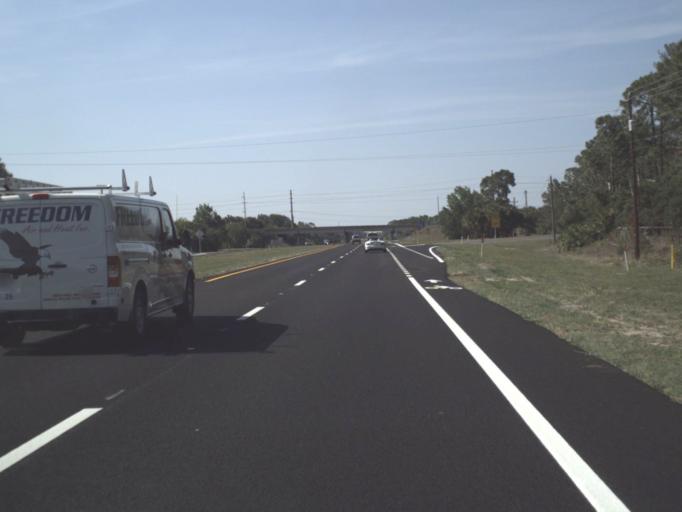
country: US
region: Florida
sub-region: Brevard County
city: Port Saint John
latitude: 28.5242
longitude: -80.7882
